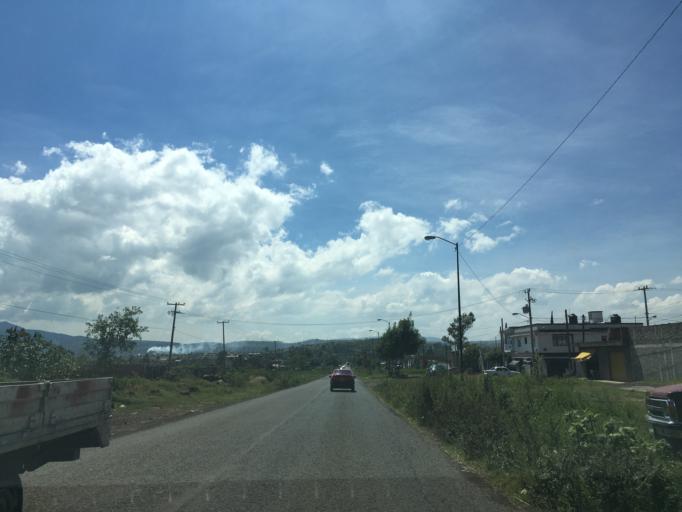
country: MX
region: Michoacan
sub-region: Morelia
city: Villas de la Loma
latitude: 19.6848
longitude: -101.2793
